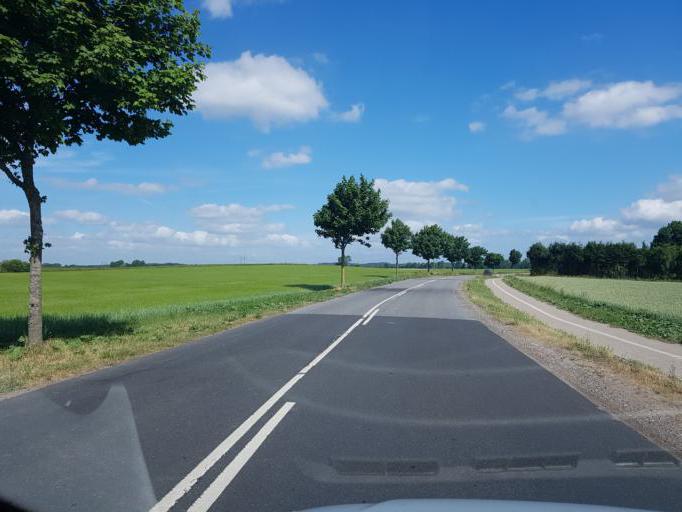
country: DK
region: Zealand
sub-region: Lejre Kommune
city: Osted
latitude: 55.5736
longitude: 11.9671
